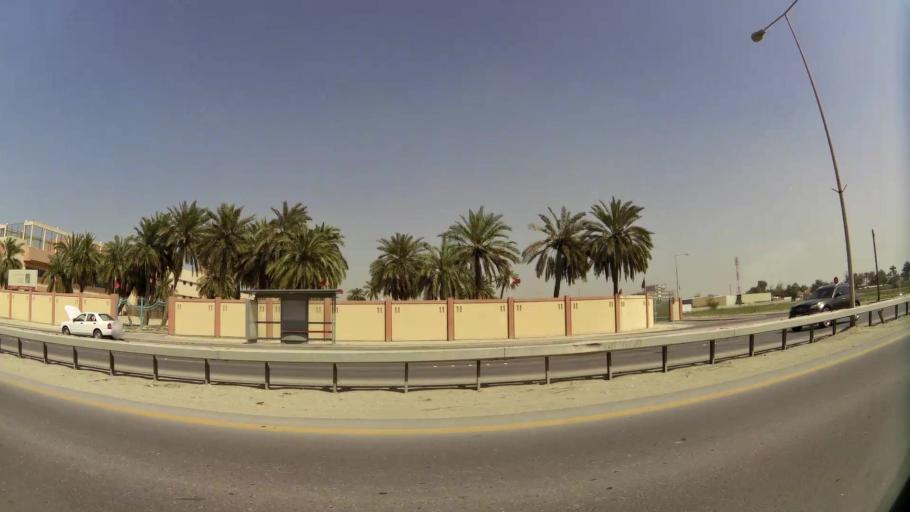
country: BH
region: Manama
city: Jidd Hafs
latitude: 26.2053
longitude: 50.4584
